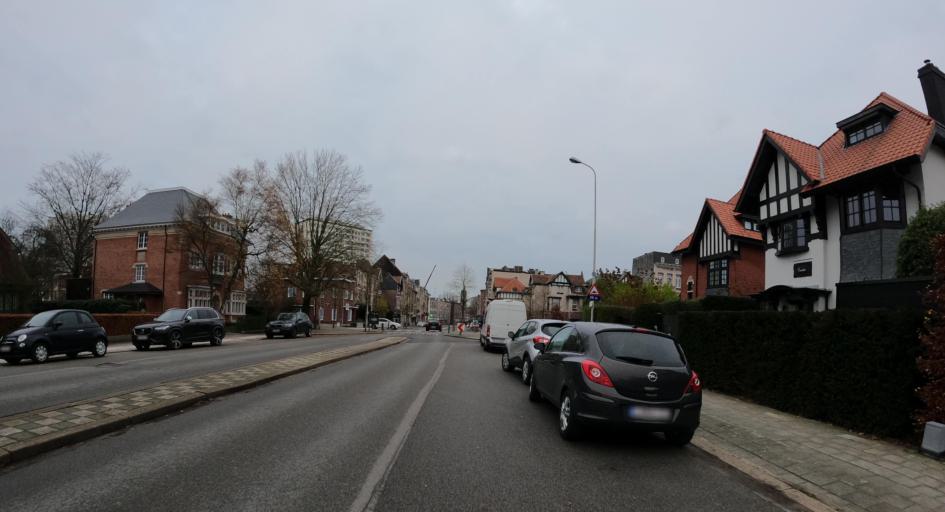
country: BE
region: Flanders
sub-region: Provincie Antwerpen
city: Antwerpen
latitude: 51.1815
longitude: 4.3952
